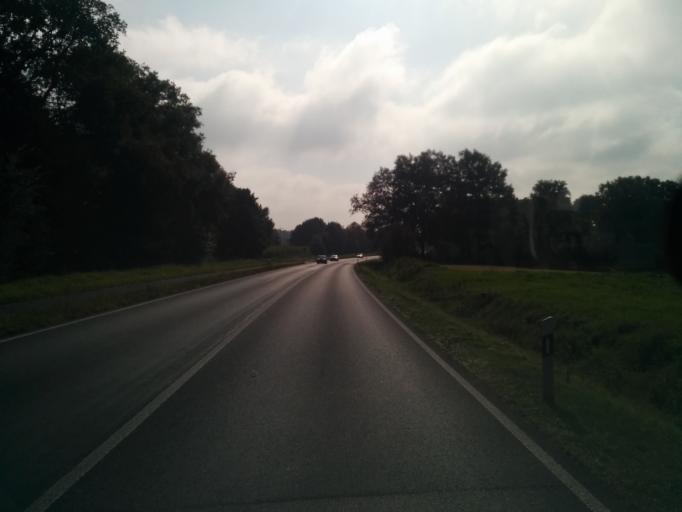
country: DE
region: North Rhine-Westphalia
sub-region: Regierungsbezirk Munster
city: Dulmen
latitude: 51.8590
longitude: 7.2447
